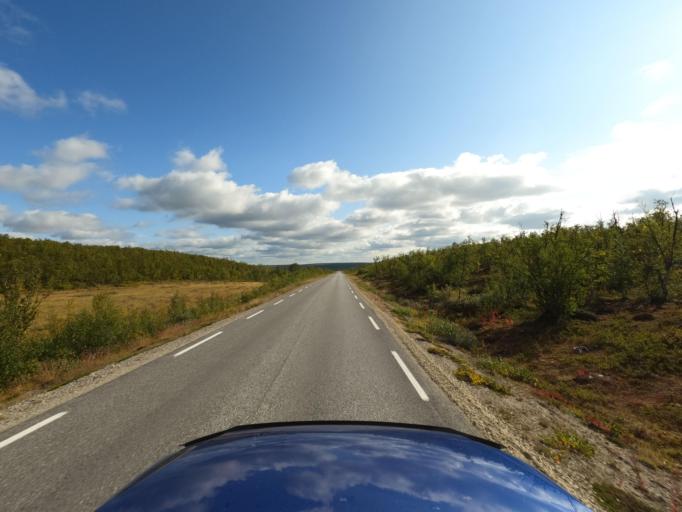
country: NO
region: Finnmark Fylke
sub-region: Porsanger
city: Lakselv
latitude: 69.3942
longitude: 24.5630
